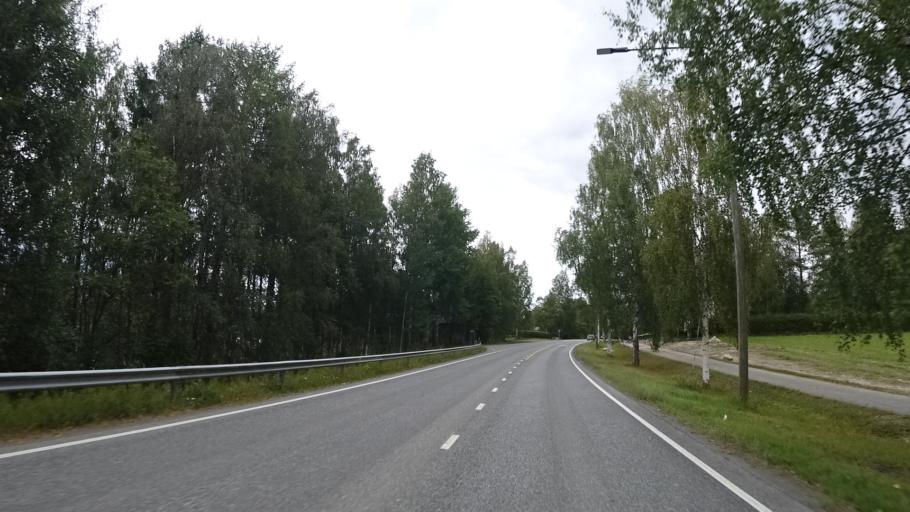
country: FI
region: North Karelia
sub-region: Joensuu
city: Ilomantsi
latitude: 62.6568
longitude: 30.9336
